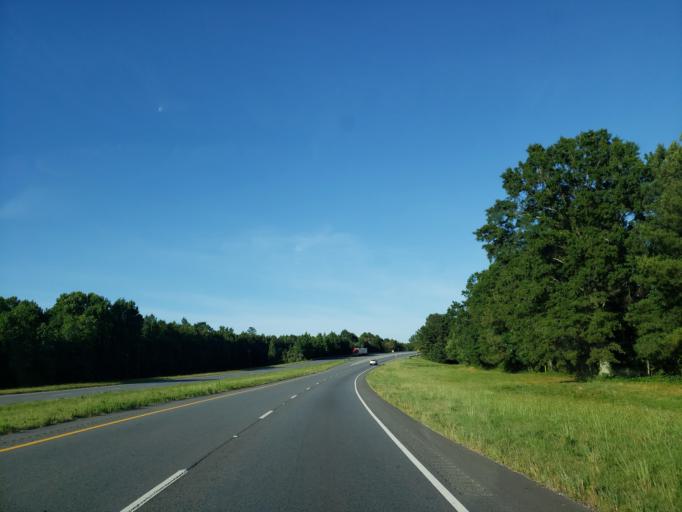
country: US
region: Georgia
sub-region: Floyd County
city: Shannon
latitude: 34.3309
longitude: -85.0956
